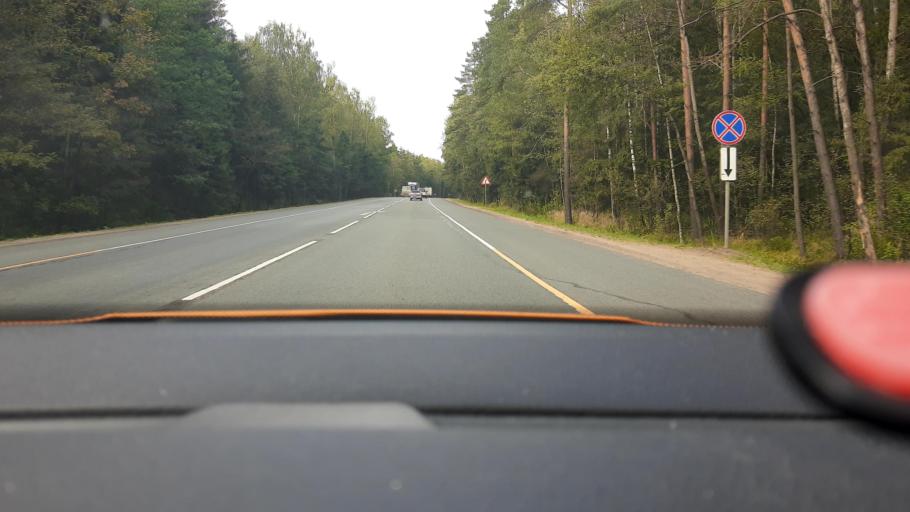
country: RU
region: Moskovskaya
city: Lesnoy
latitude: 56.0820
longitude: 38.0095
